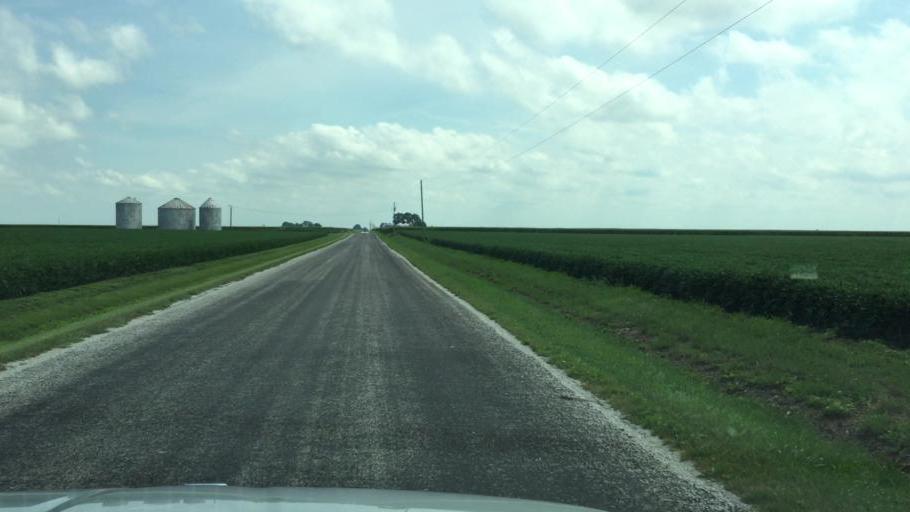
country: US
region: Illinois
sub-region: Hancock County
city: Carthage
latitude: 40.5308
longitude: -91.1770
